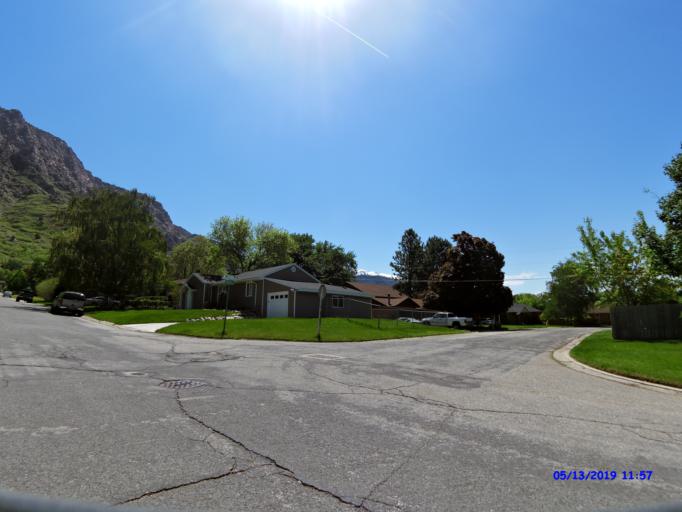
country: US
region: Utah
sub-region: Weber County
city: Harrisville
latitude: 41.2662
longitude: -111.9502
